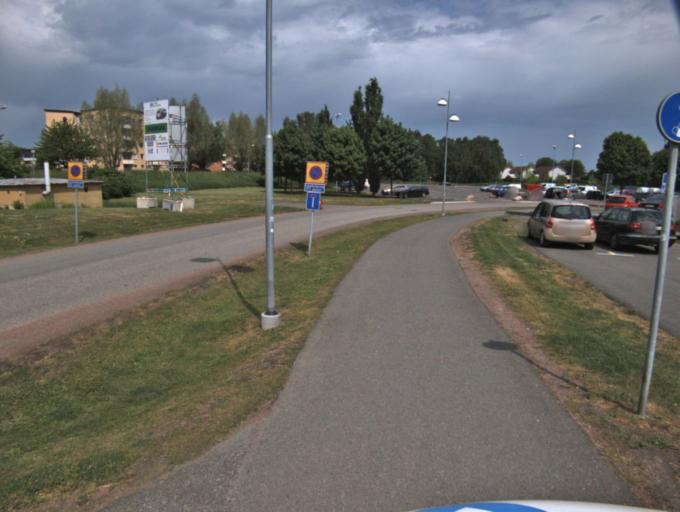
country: SE
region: Skane
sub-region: Kristianstads Kommun
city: Kristianstad
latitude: 56.0439
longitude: 14.1661
